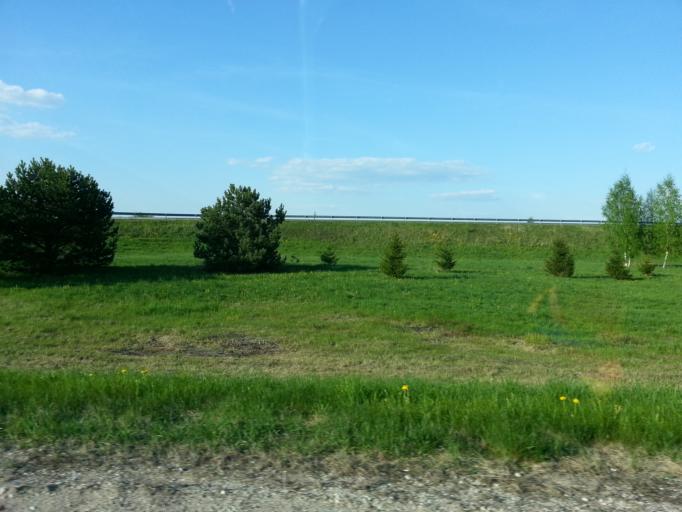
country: LT
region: Vilnius County
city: Ukmerge
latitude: 55.3972
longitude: 24.6981
